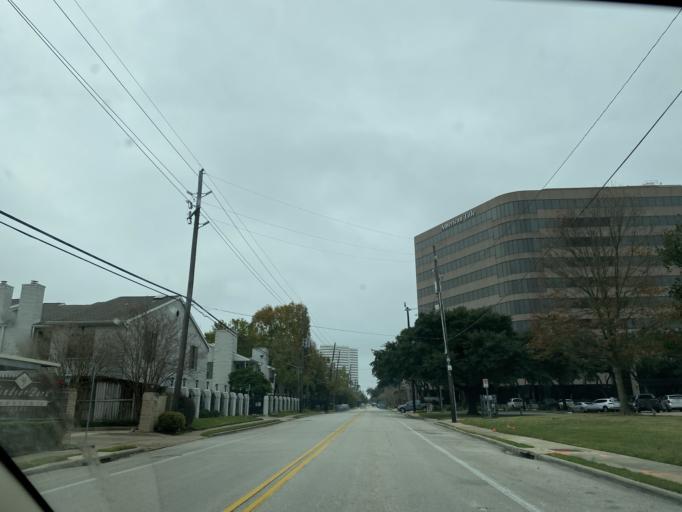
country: US
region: Texas
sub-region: Harris County
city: Hunters Creek Village
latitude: 29.7465
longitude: -95.4795
